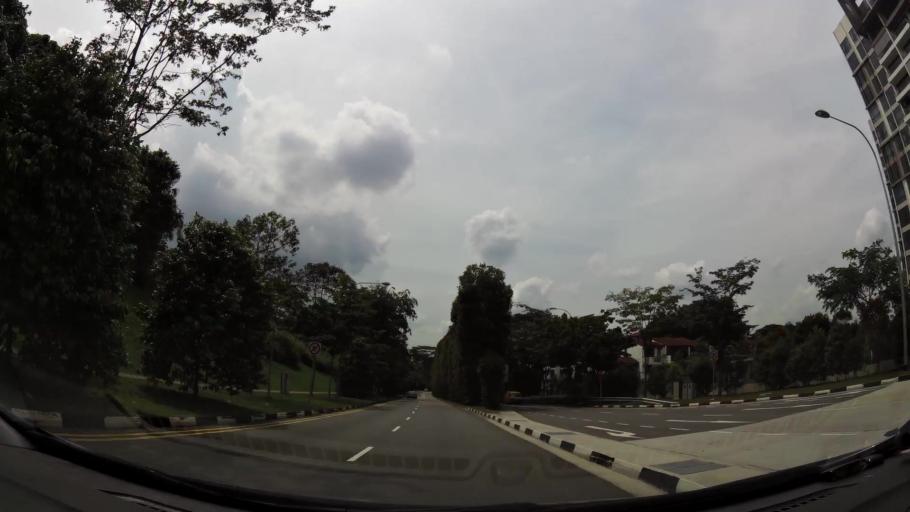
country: MY
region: Johor
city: Johor Bahru
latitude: 1.3645
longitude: 103.7719
